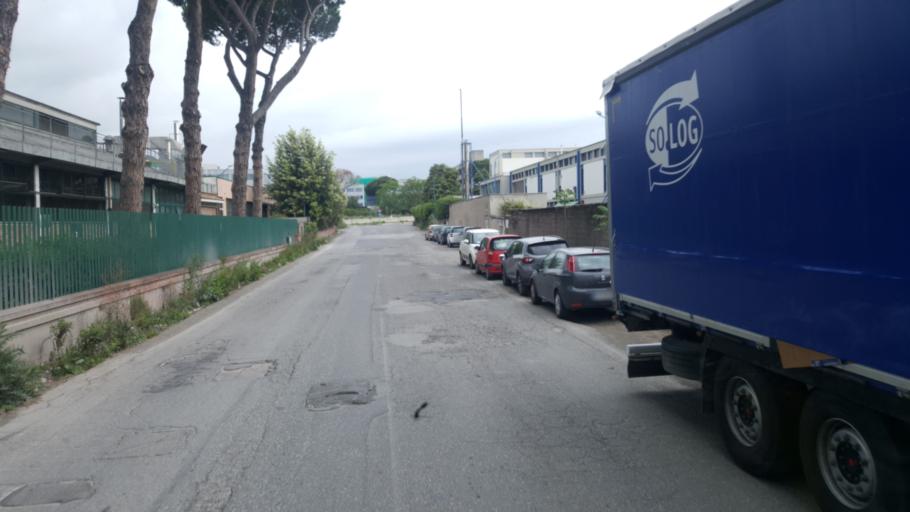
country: IT
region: Latium
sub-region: Citta metropolitana di Roma Capitale
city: Setteville
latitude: 41.9348
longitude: 12.6147
